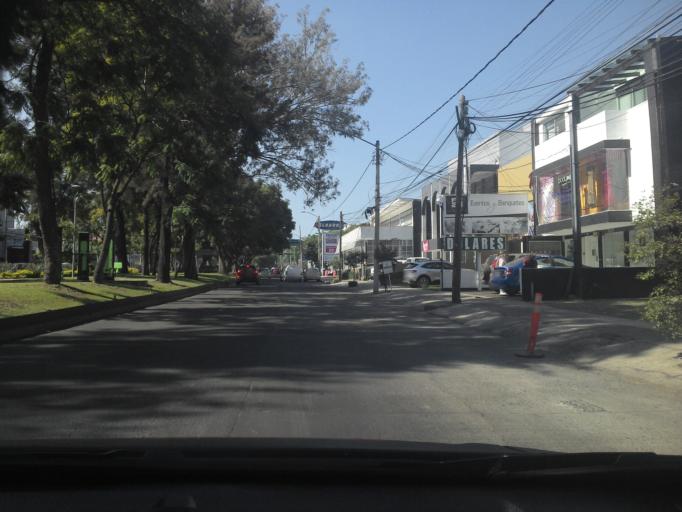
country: MX
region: Jalisco
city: Zapopan2
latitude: 20.6977
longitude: -103.3884
